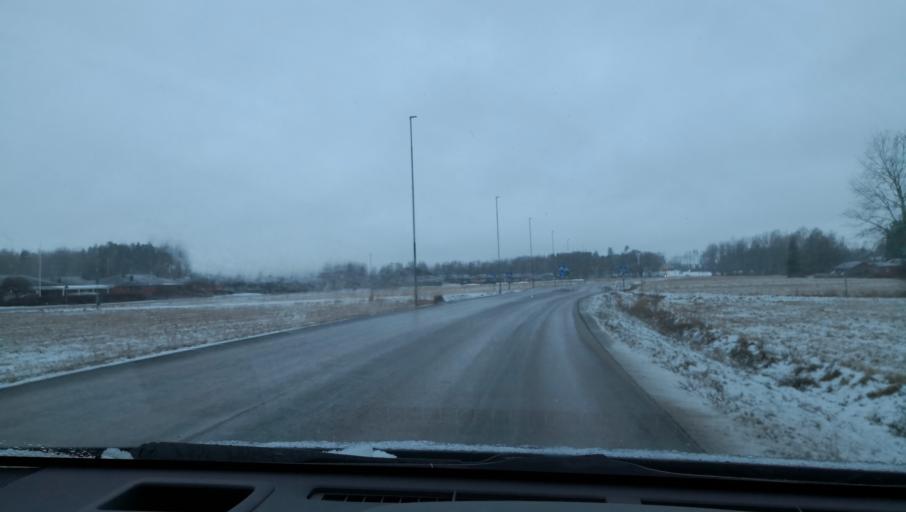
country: SE
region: Vaestmanland
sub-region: Hallstahammars Kommun
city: Hallstahammar
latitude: 59.6062
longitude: 16.2125
